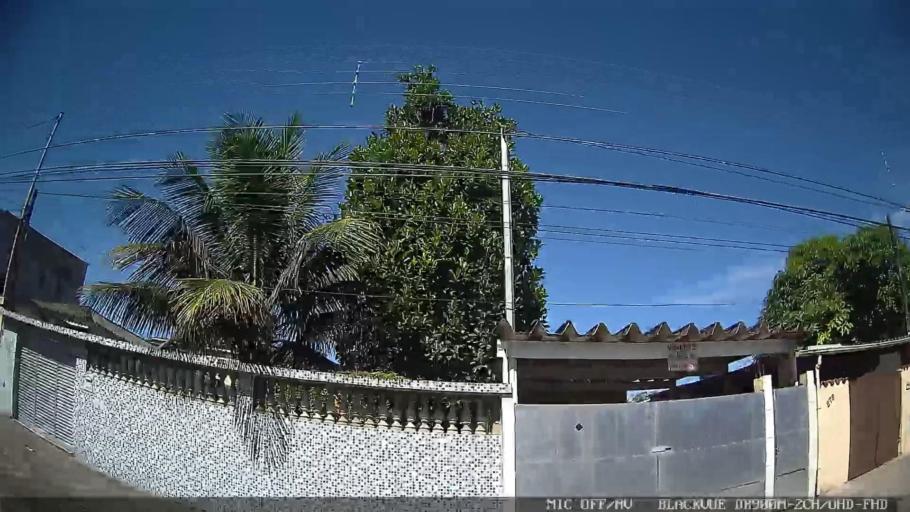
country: BR
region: Sao Paulo
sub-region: Guaruja
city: Guaruja
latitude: -23.9623
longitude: -46.2813
